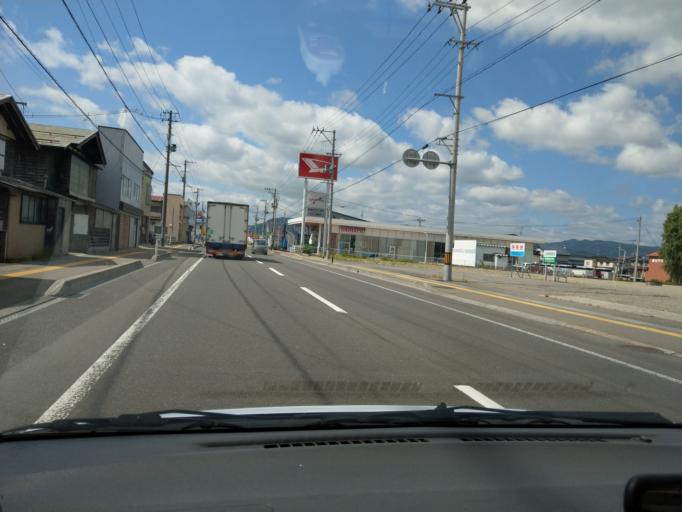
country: JP
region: Akita
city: Yuzawa
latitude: 39.1718
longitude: 140.4912
